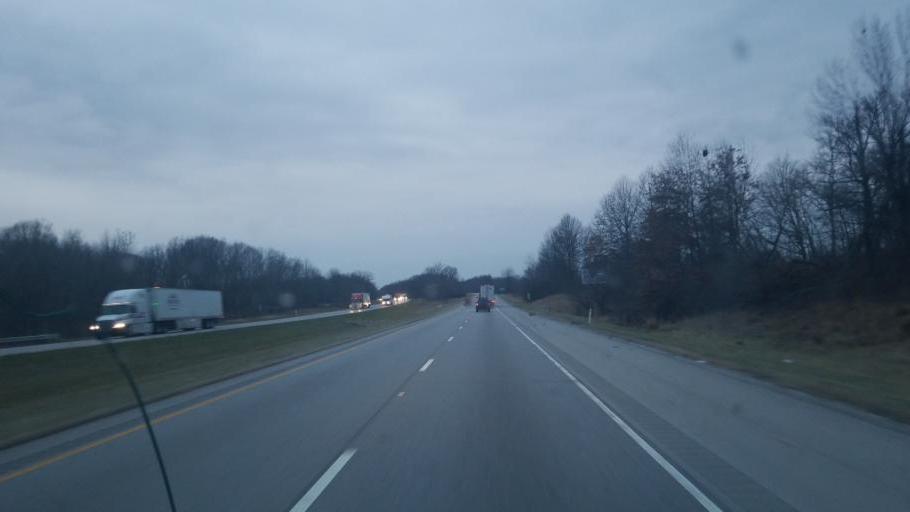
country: US
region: Indiana
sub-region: Vigo County
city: Seelyville
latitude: 39.4460
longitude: -87.2467
